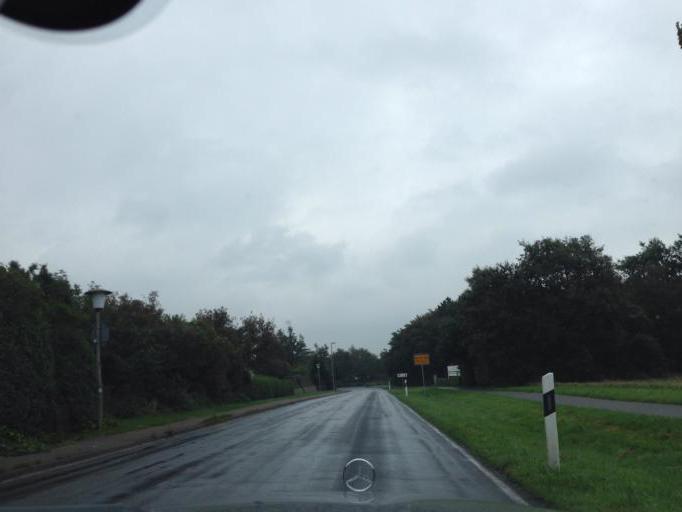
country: DE
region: Schleswig-Holstein
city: Wrixum
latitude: 54.6947
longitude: 8.5535
